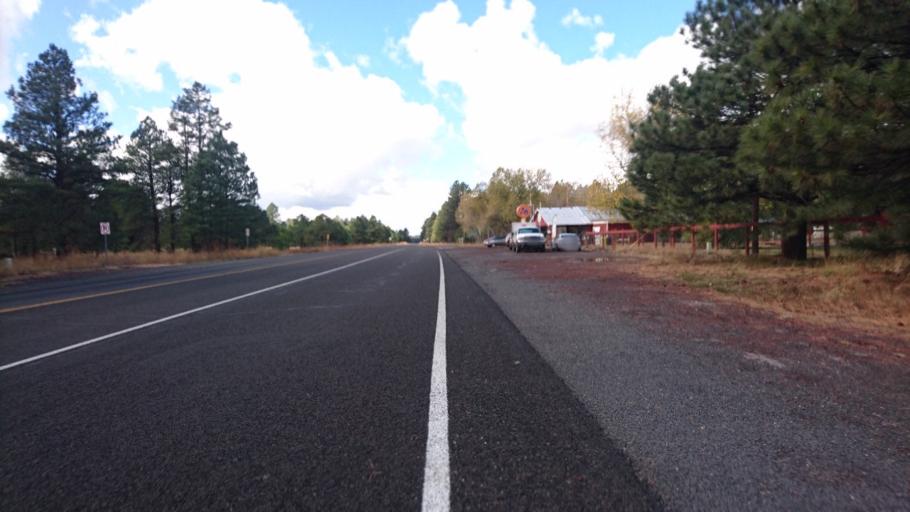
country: US
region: Arizona
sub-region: Coconino County
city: Parks
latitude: 35.2600
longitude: -111.9478
